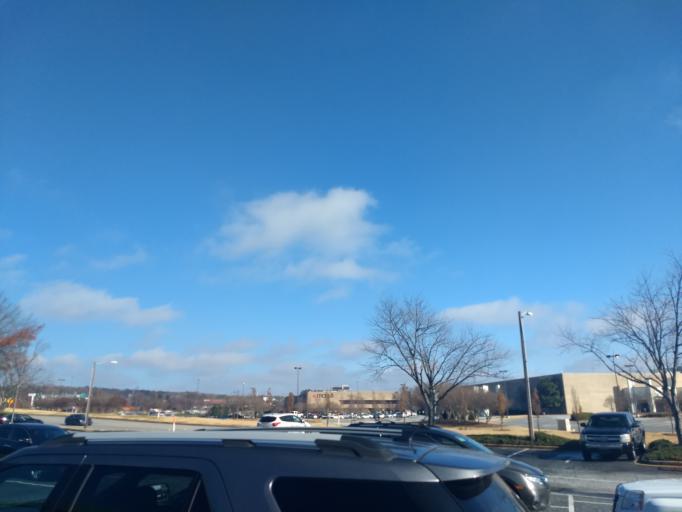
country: US
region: South Carolina
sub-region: Greenville County
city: Wade Hampton
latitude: 34.8479
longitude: -82.3368
